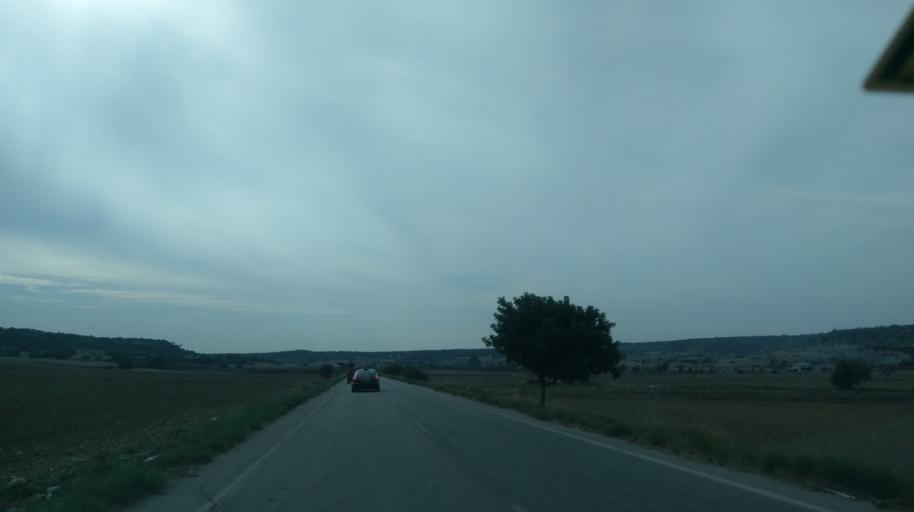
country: CY
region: Ammochostos
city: Leonarisso
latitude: 35.4621
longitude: 34.1365
